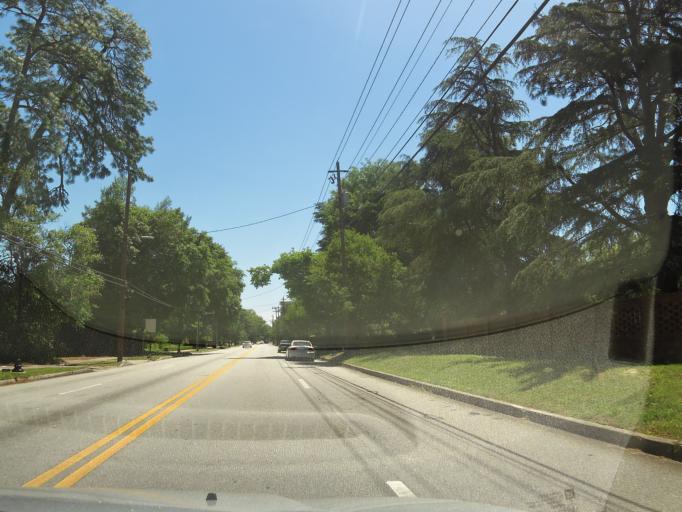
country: US
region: Georgia
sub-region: Richmond County
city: Augusta
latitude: 33.4782
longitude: -82.0222
